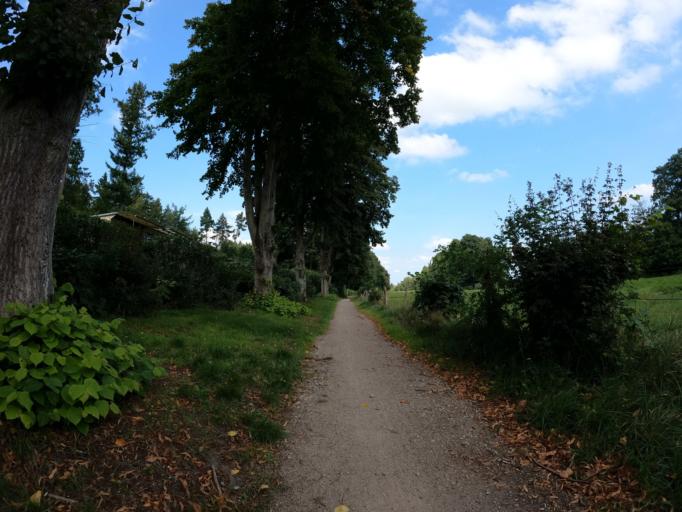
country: DE
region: Mecklenburg-Vorpommern
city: Malchow
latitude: 53.4895
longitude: 12.4354
